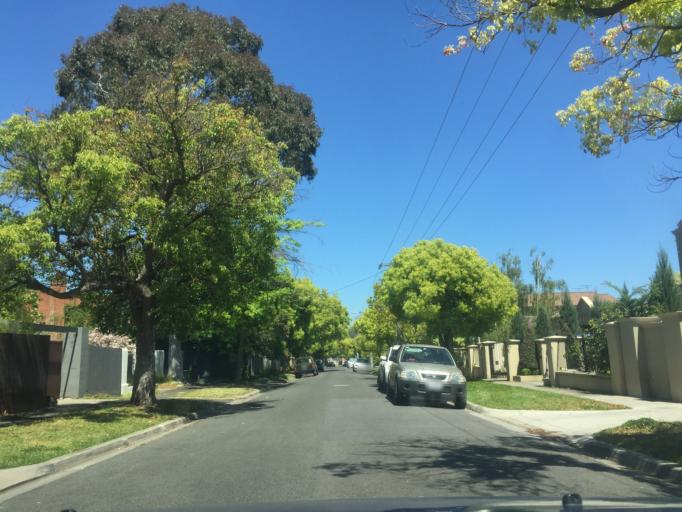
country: AU
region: Victoria
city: Balwyn
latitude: -37.8205
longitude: 145.0723
